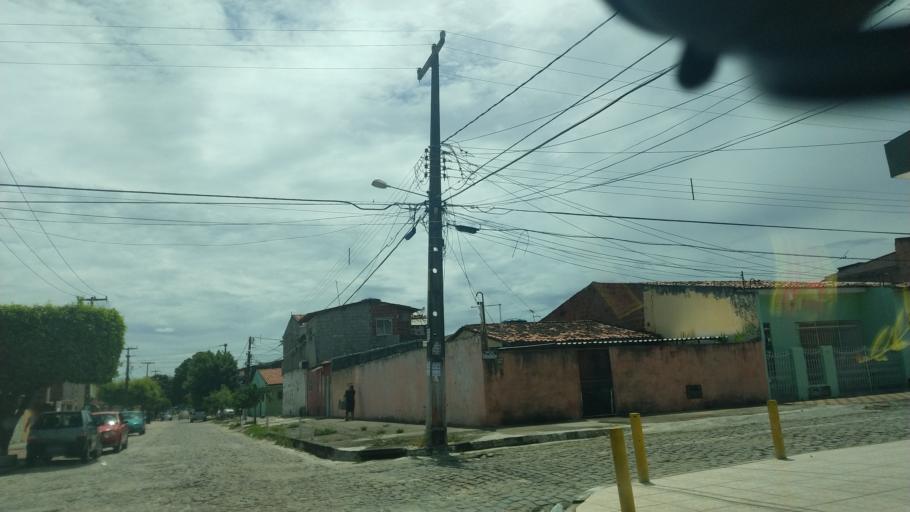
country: BR
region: Rio Grande do Norte
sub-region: Natal
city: Natal
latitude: -5.8246
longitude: -35.2389
